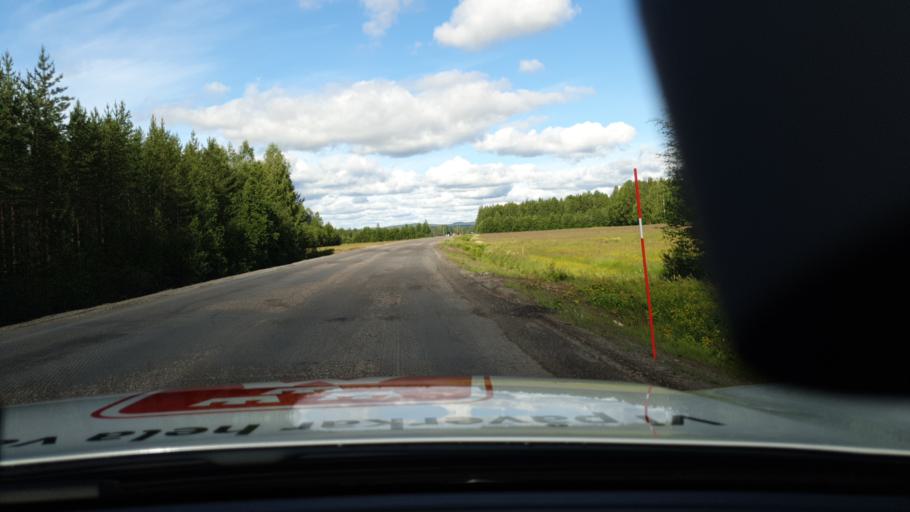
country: SE
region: Norrbotten
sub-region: Bodens Kommun
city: Boden
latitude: 65.8498
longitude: 21.5351
